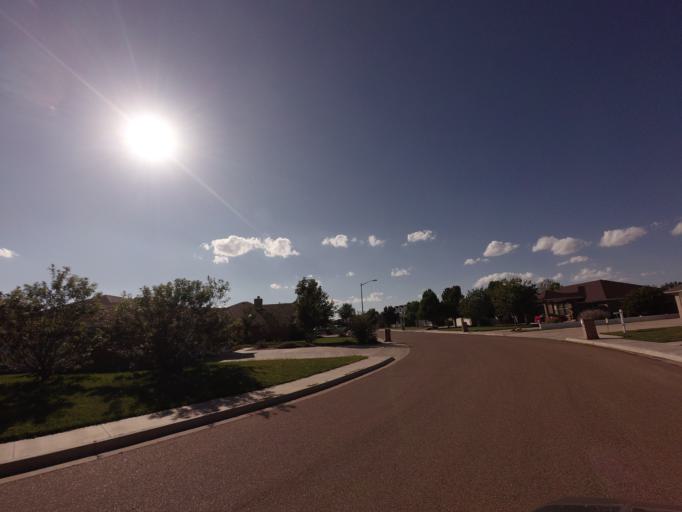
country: US
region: New Mexico
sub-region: Curry County
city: Clovis
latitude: 34.4404
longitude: -103.1755
